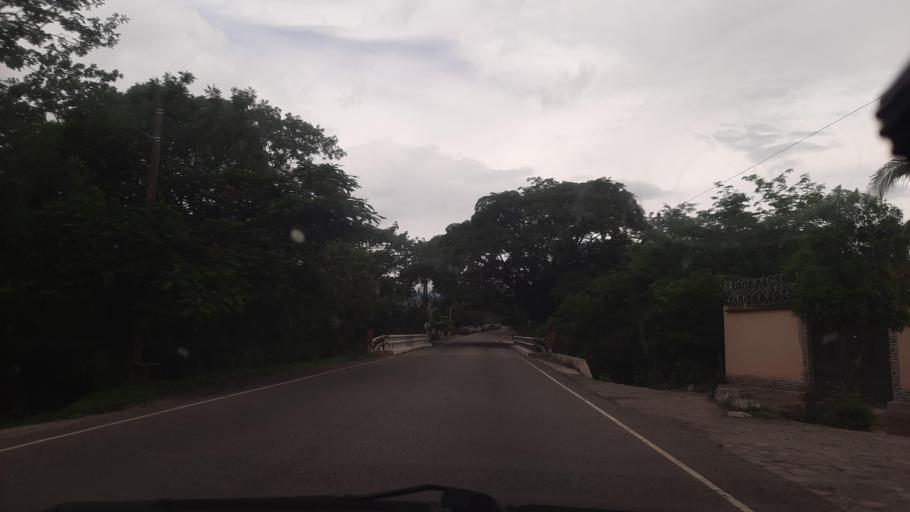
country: GT
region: Zacapa
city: San Jorge
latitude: 14.9064
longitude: -89.5263
